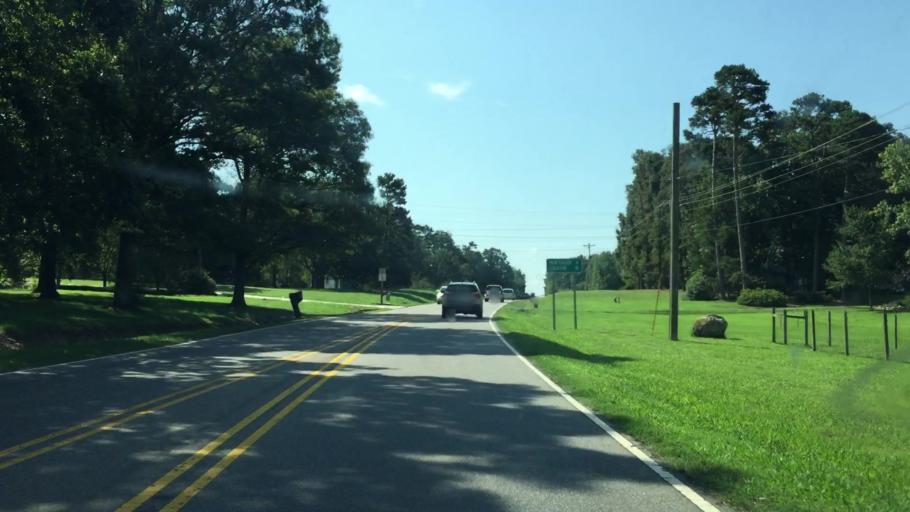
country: US
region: North Carolina
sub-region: Union County
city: Unionville
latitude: 35.1278
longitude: -80.4314
